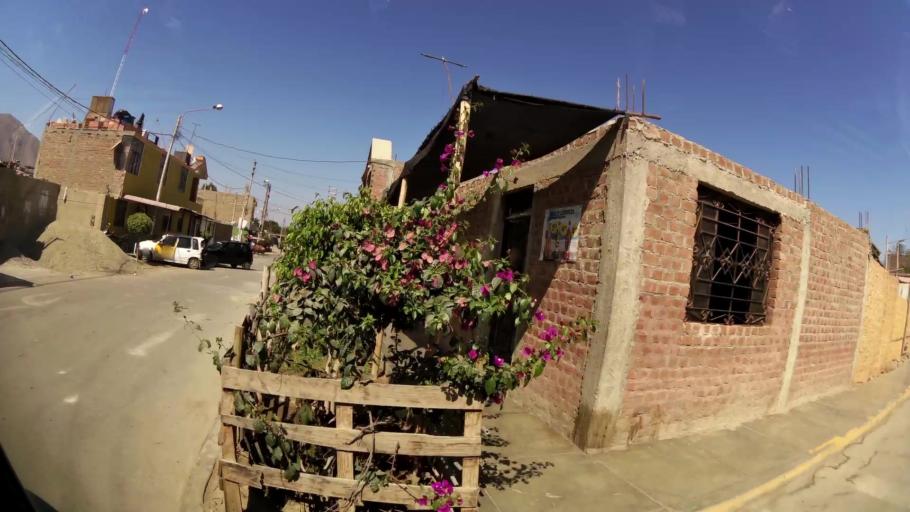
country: PE
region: Ica
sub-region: Provincia de Ica
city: San Juan Bautista
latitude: -13.9607
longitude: -75.6950
